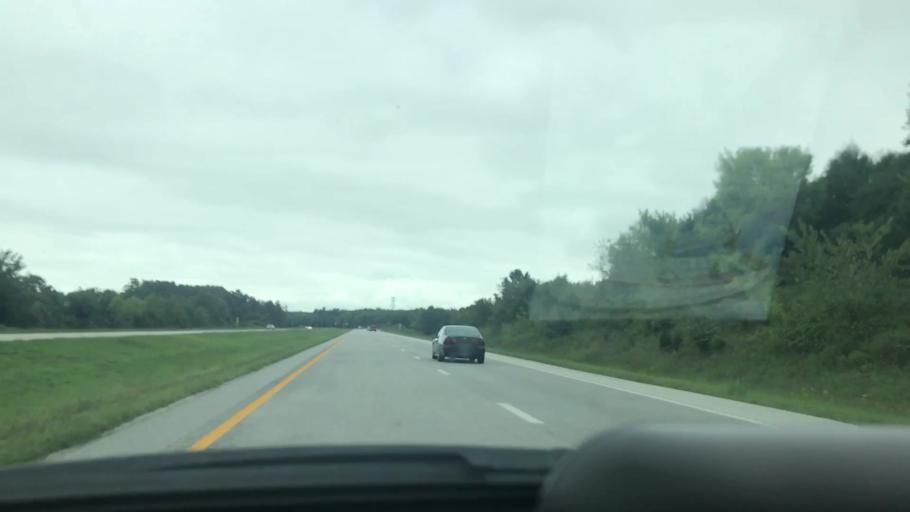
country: US
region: Missouri
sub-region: Greene County
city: Strafford
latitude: 37.3153
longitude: -93.1704
